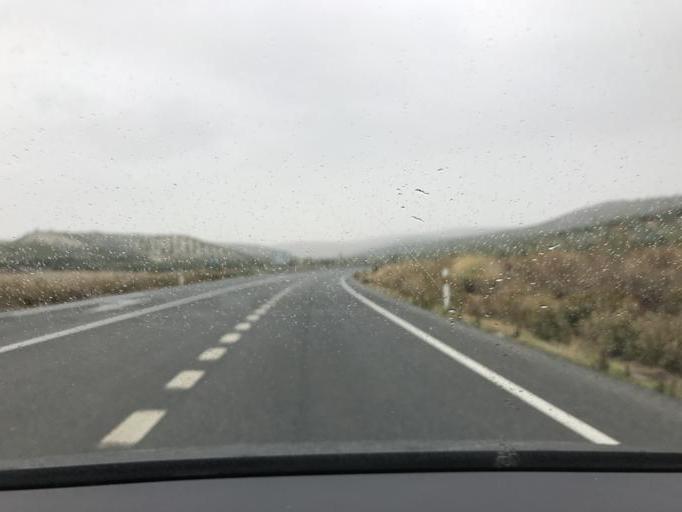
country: ES
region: Andalusia
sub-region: Provincia de Granada
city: Las Gabias
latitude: 37.1594
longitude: -3.7259
